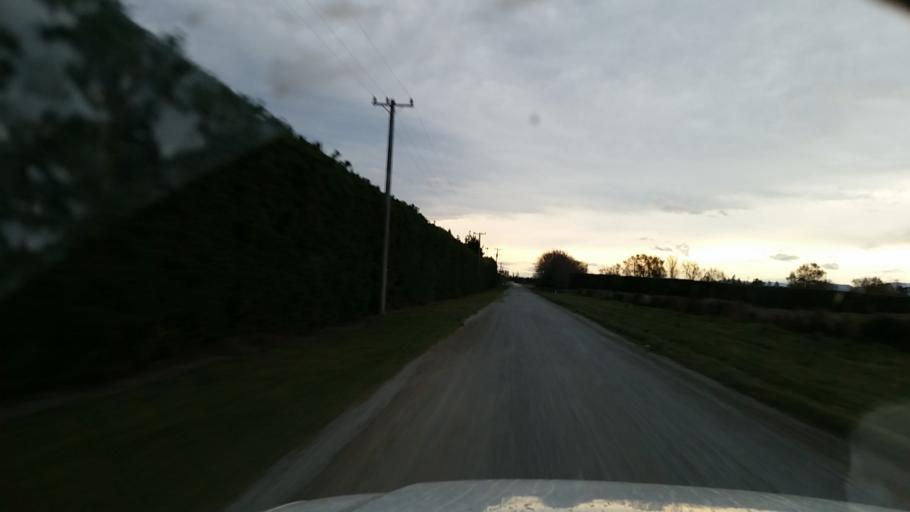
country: NZ
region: Canterbury
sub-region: Ashburton District
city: Ashburton
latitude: -43.8327
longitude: 171.6235
